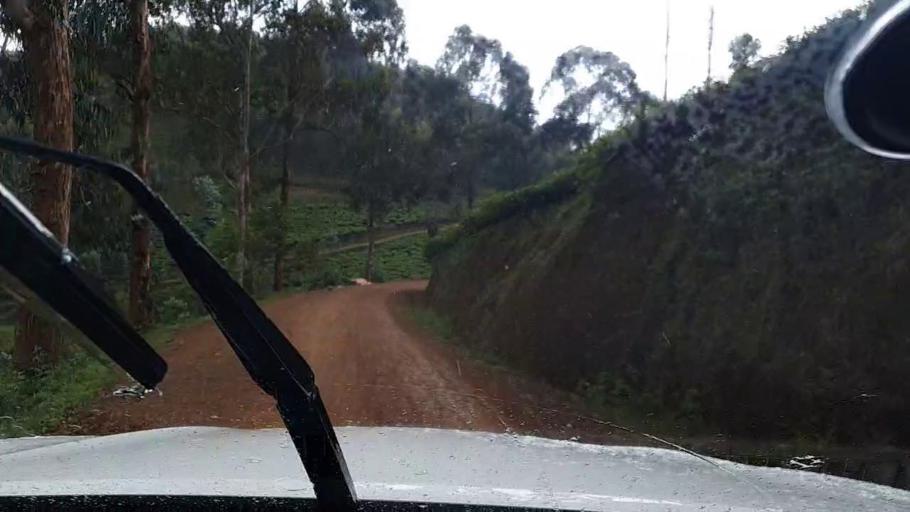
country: RW
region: Western Province
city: Kibuye
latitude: -2.1562
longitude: 29.4309
